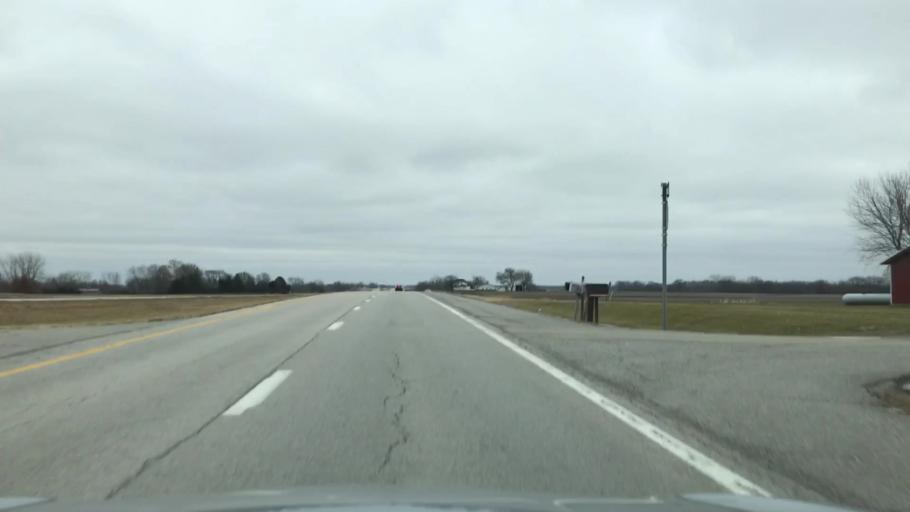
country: US
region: Missouri
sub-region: Livingston County
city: Chillicothe
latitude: 39.7759
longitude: -93.4948
